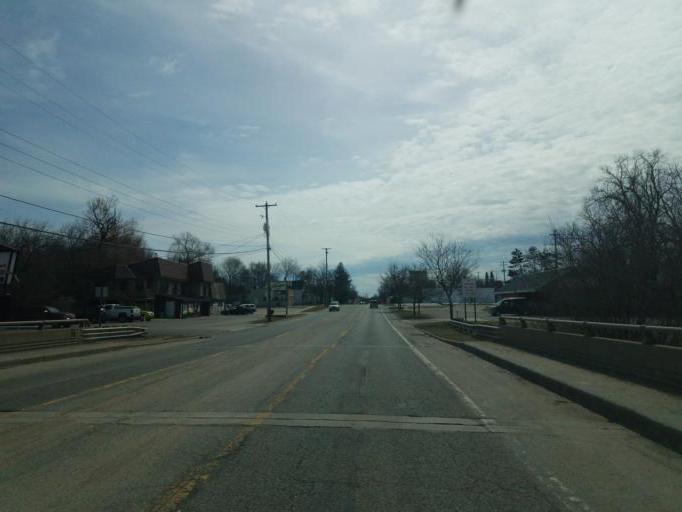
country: US
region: Michigan
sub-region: Osceola County
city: Reed City
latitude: 43.8822
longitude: -85.5104
